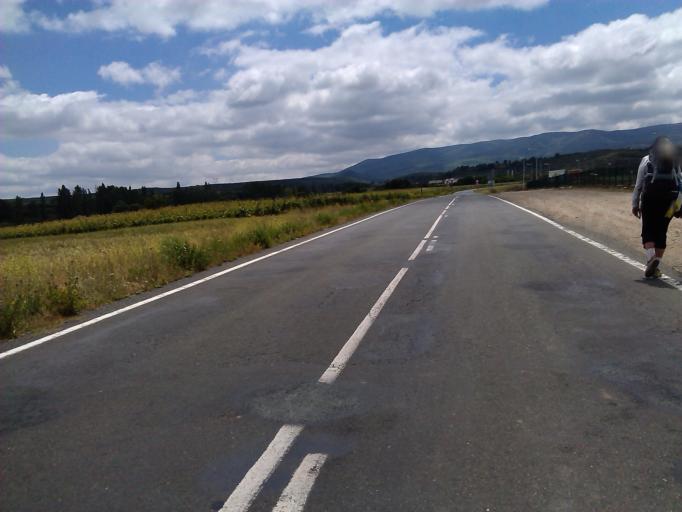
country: ES
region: La Rioja
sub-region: Provincia de La Rioja
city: Hornos de Moncalvillo
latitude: 42.4148
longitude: -2.5925
